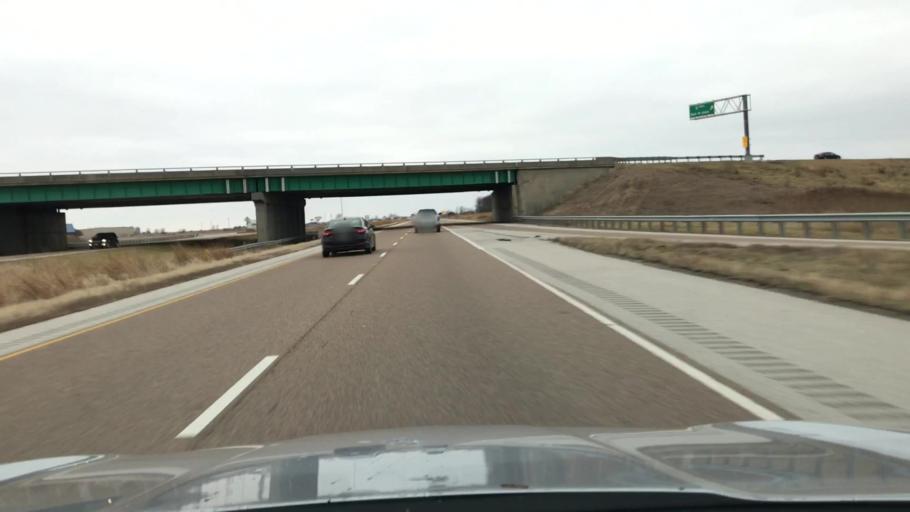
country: US
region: Illinois
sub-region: Montgomery County
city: Litchfield
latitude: 39.1764
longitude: -89.6808
